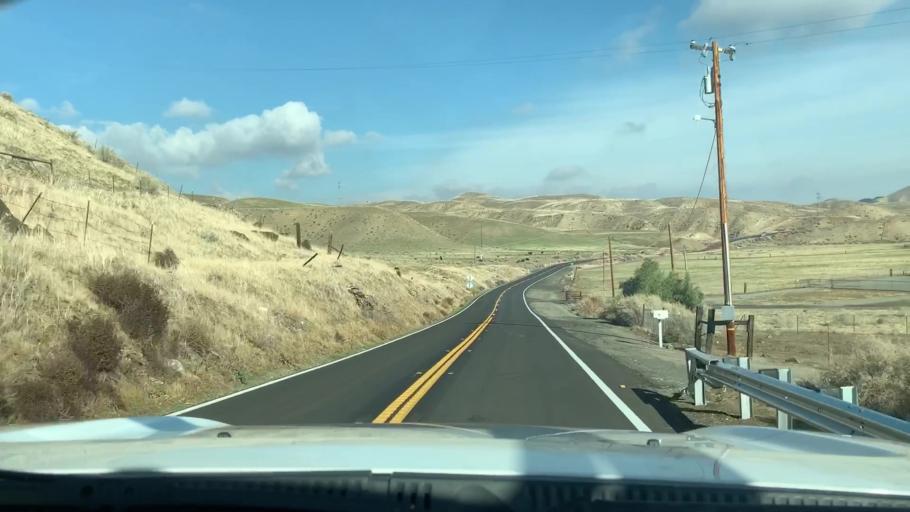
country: US
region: California
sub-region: Fresno County
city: Coalinga
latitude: 36.0929
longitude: -120.4242
